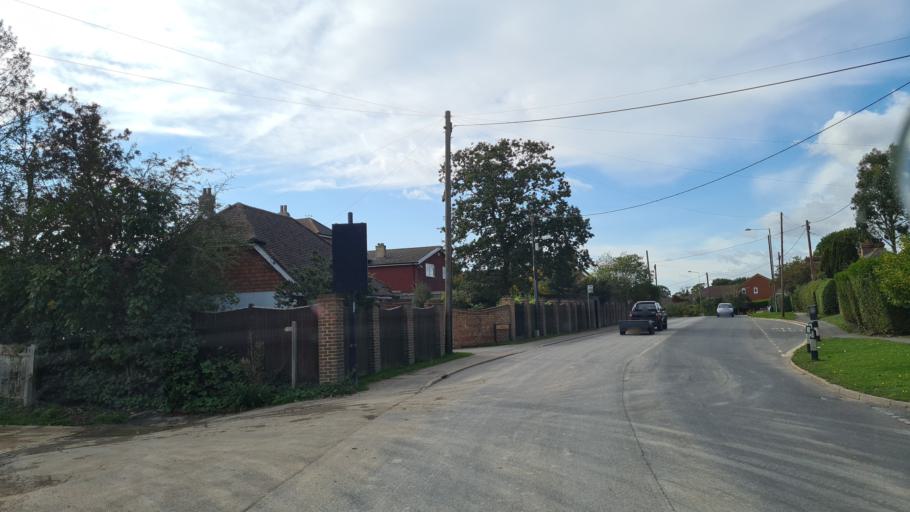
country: GB
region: England
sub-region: East Sussex
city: Hailsham
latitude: 50.8777
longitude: 0.2678
